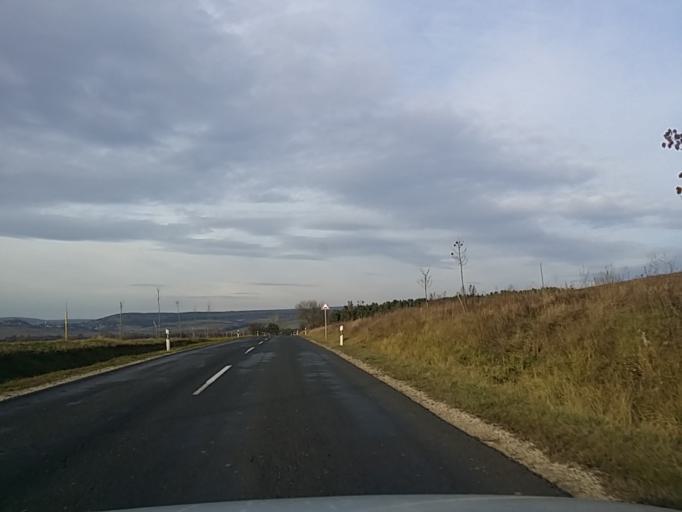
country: HU
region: Veszprem
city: Urkut
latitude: 46.9746
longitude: 17.6271
